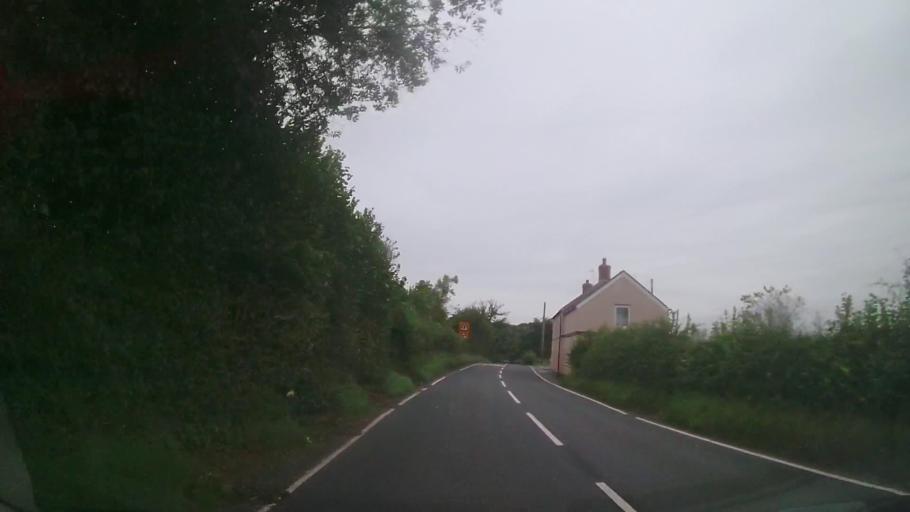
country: GB
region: Wales
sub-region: Carmarthenshire
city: Saint Clears
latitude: 51.8064
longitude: -4.4970
